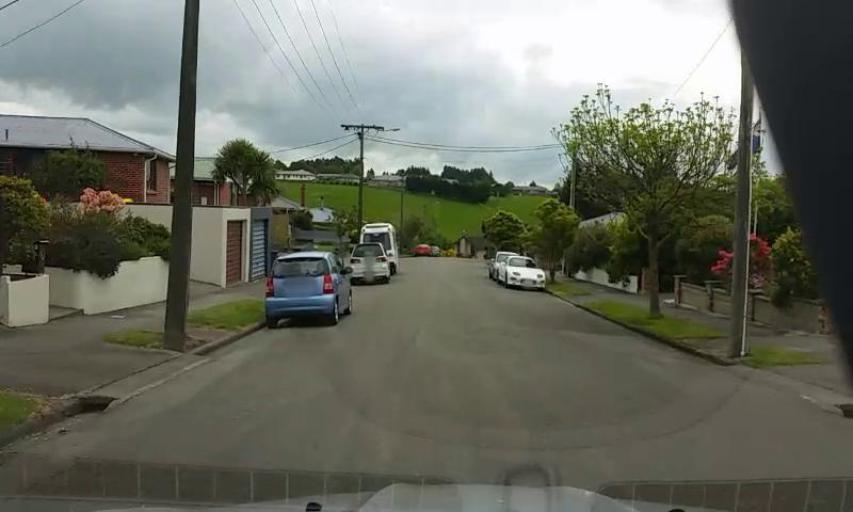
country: NZ
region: Canterbury
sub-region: Timaru District
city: Timaru
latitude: -44.3746
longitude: 171.2346
